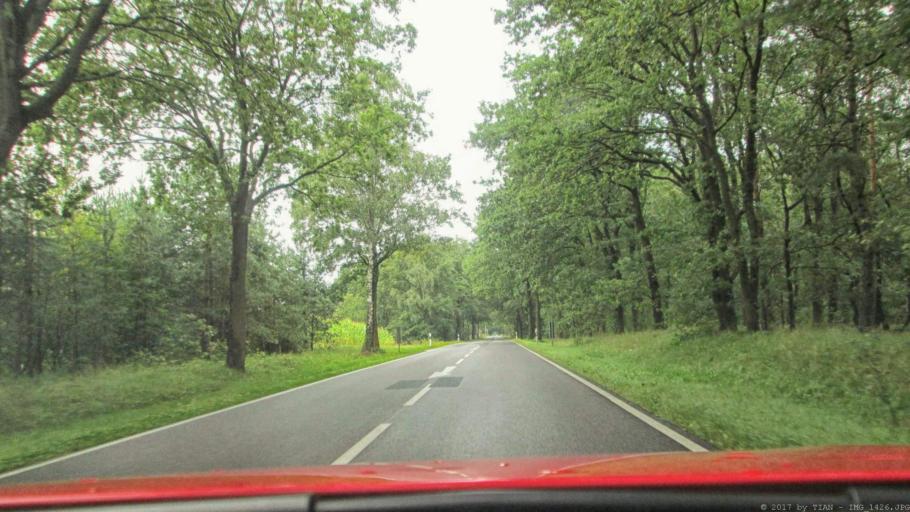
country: DE
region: Lower Saxony
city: Wittingen
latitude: 52.7719
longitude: 10.7123
